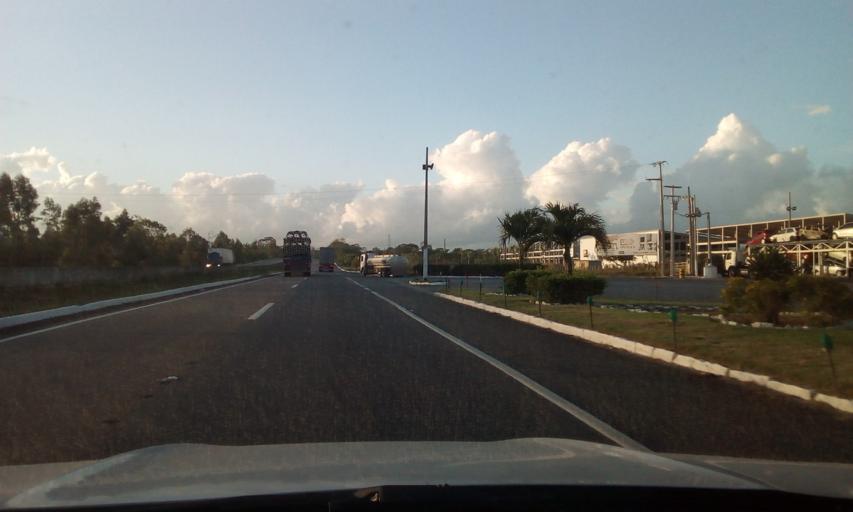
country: BR
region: Paraiba
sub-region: Conde
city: Conde
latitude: -7.2898
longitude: -34.9383
